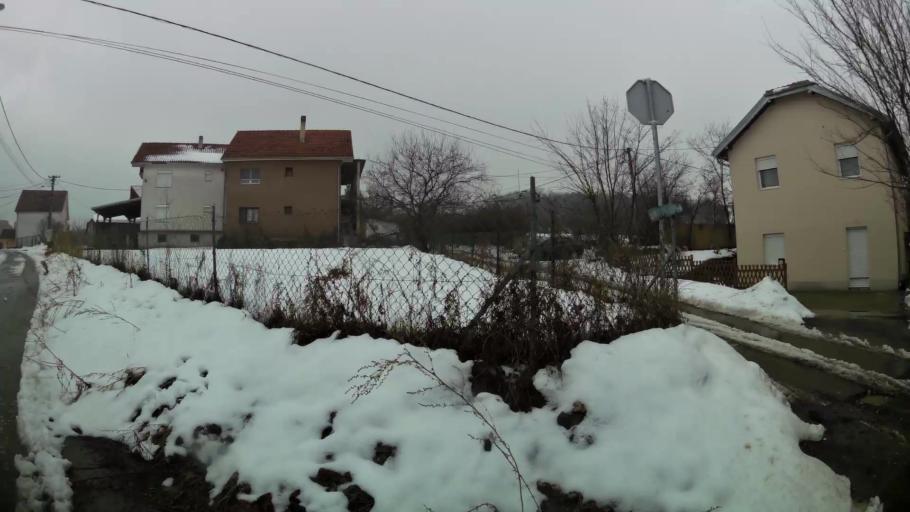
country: RS
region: Central Serbia
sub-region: Belgrade
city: Zvezdara
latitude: 44.7529
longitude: 20.5228
